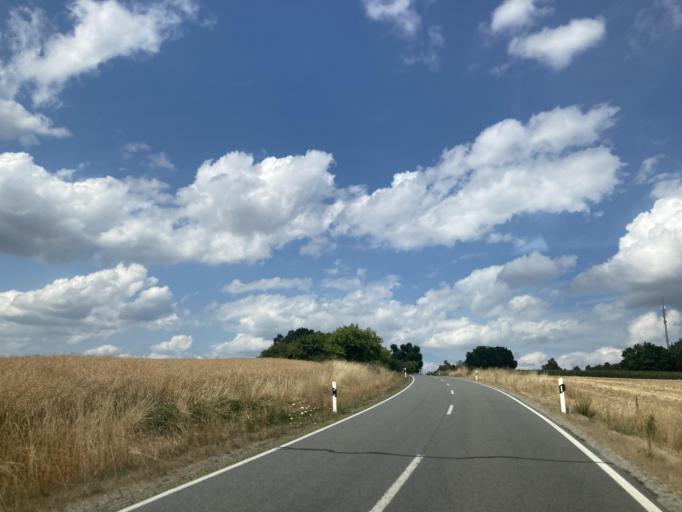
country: DE
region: Hesse
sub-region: Regierungsbezirk Kassel
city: Grossenluder
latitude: 50.5428
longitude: 9.5270
